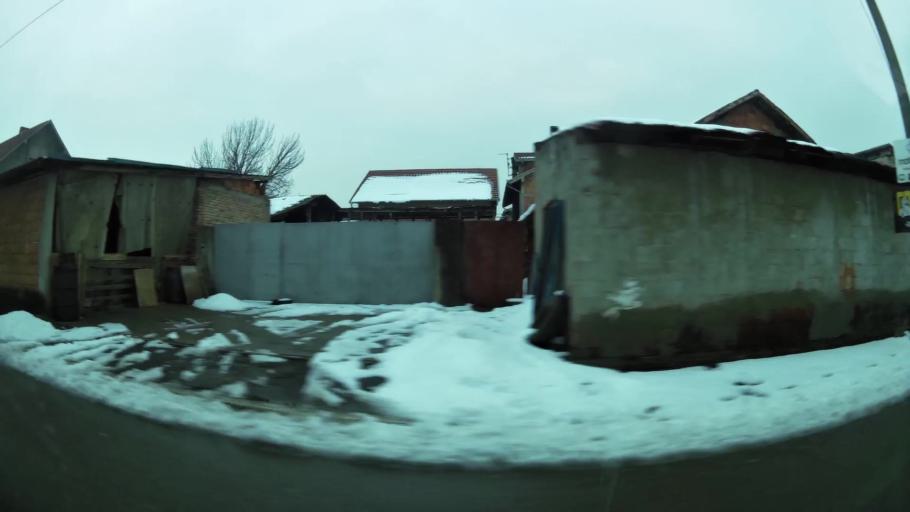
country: RS
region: Central Serbia
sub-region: Belgrade
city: Zemun
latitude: 44.8122
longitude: 20.3781
